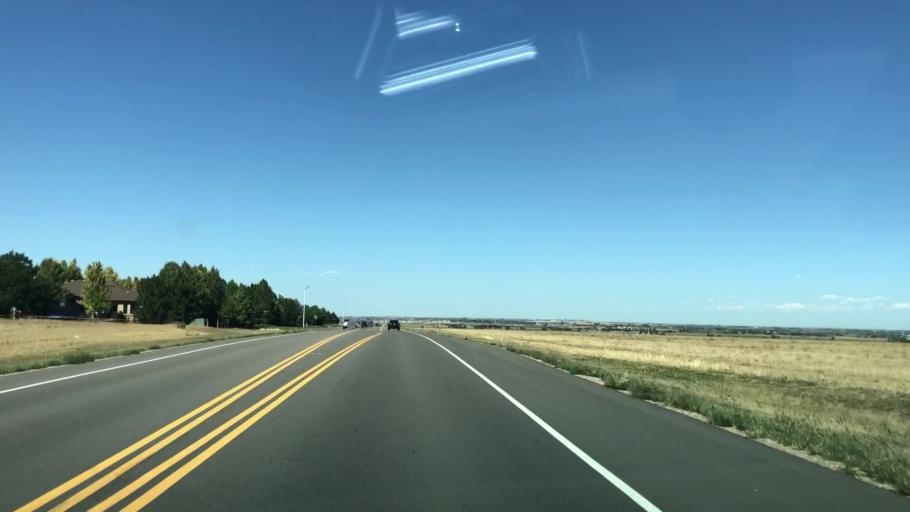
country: US
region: Colorado
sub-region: Weld County
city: Windsor
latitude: 40.4602
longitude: -104.9442
